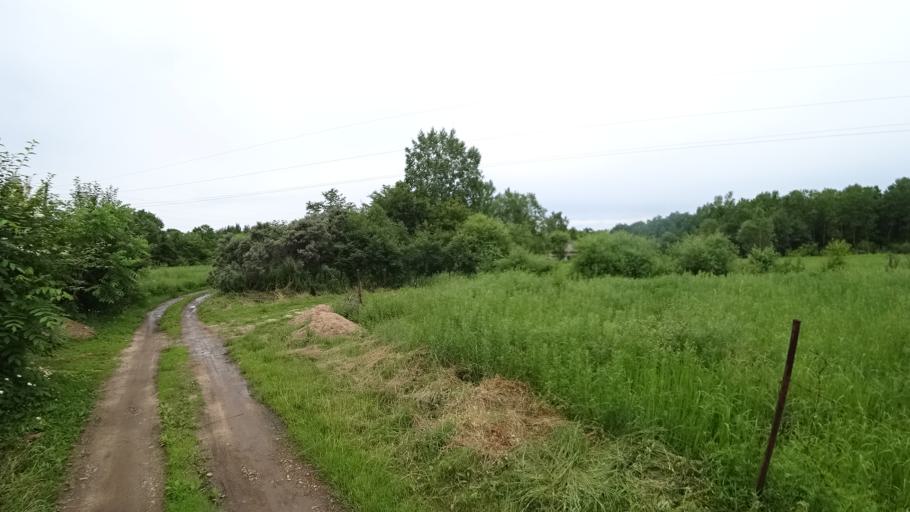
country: RU
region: Primorskiy
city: Novosysoyevka
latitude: 44.2040
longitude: 133.3282
